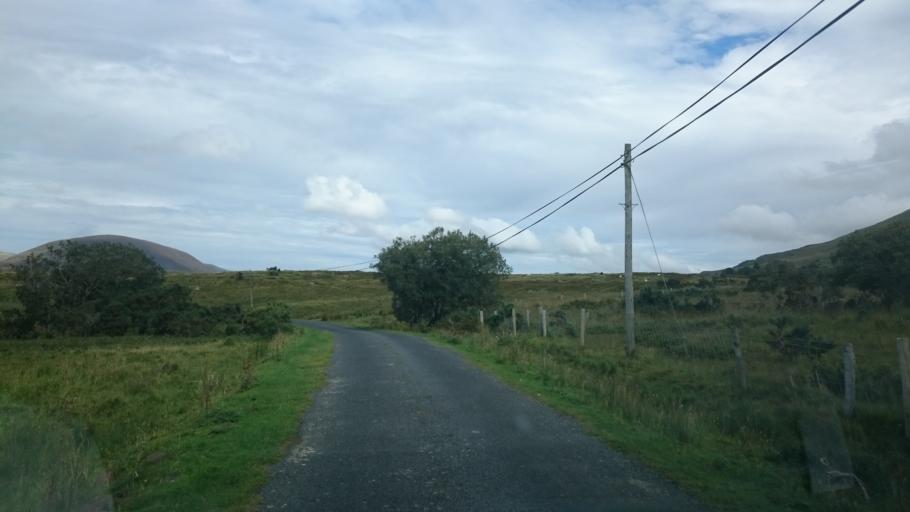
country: IE
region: Connaught
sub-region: Maigh Eo
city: Westport
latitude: 53.9336
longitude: -9.5627
